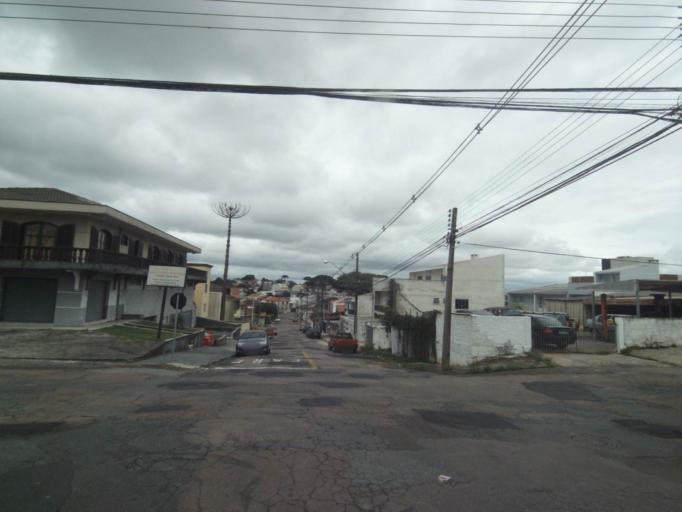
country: BR
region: Parana
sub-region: Curitiba
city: Curitiba
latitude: -25.4878
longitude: -49.2897
